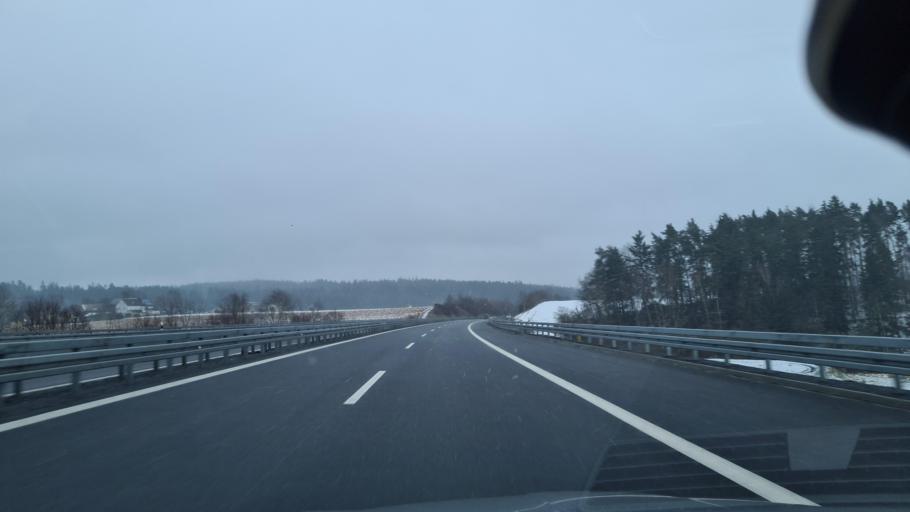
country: DE
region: Bavaria
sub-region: Upper Palatinate
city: Pechbrunn
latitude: 49.9787
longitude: 12.1679
